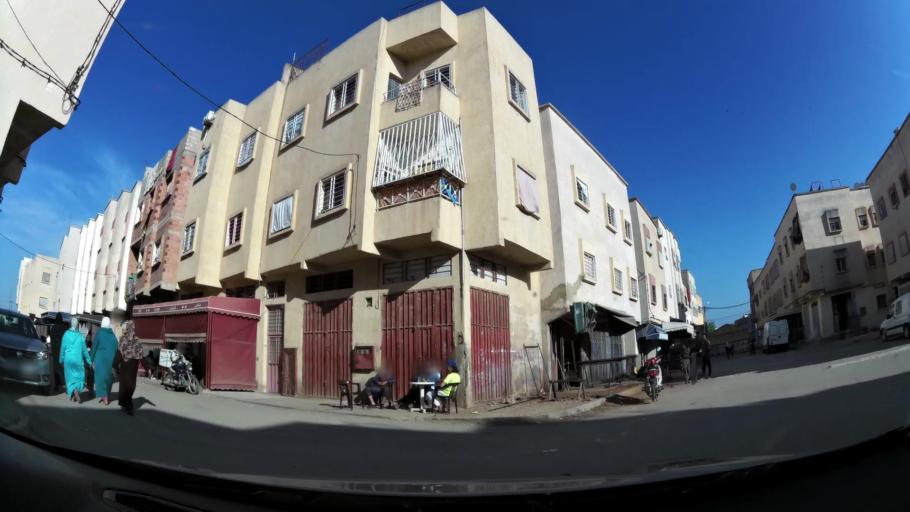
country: MA
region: Fes-Boulemane
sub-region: Fes
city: Fes
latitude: 34.0188
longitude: -5.0389
